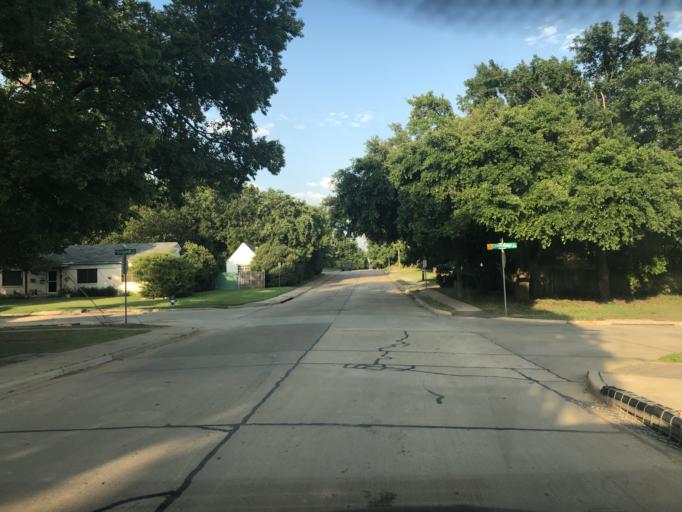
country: US
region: Texas
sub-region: Dallas County
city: Irving
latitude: 32.7975
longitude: -96.9546
